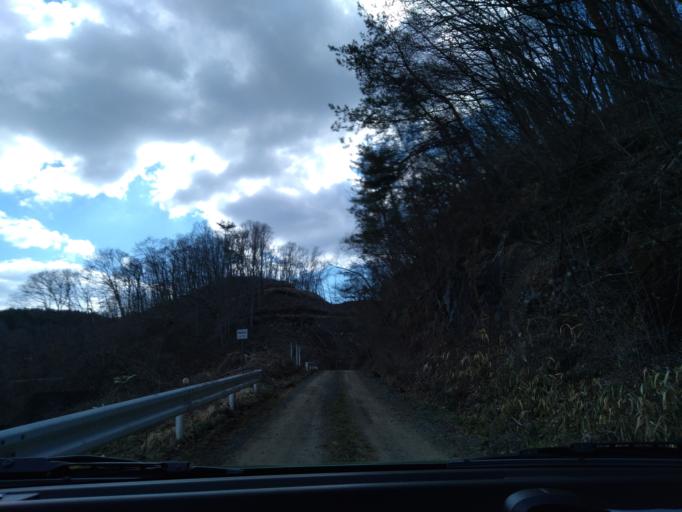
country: JP
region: Iwate
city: Ichinoseki
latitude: 38.9869
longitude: 141.0317
